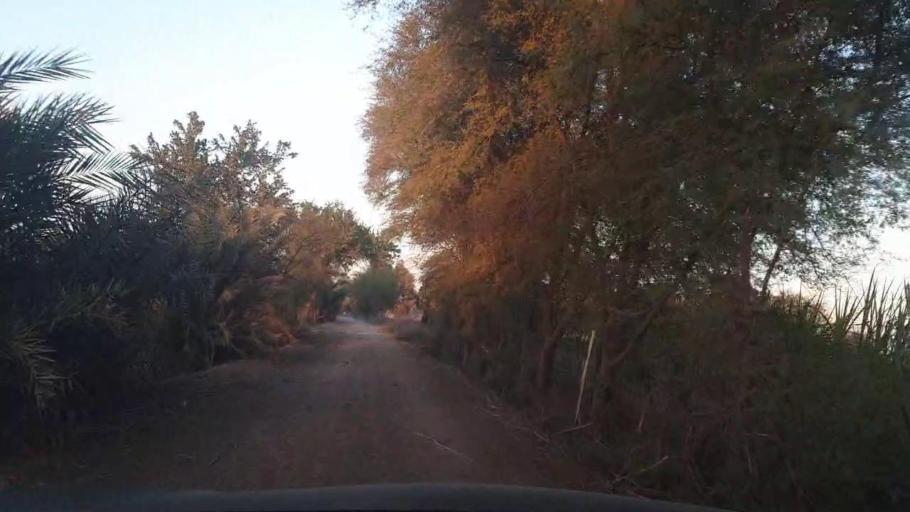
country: PK
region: Sindh
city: Ghotki
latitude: 28.0593
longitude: 69.3681
